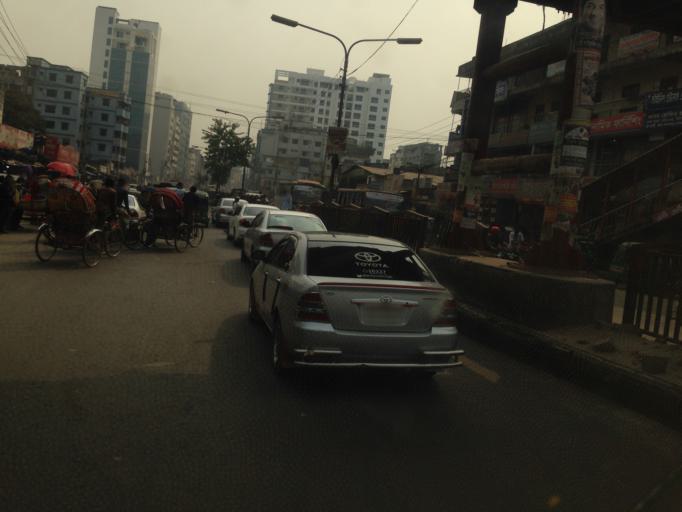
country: BD
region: Dhaka
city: Paltan
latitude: 23.7861
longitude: 90.4257
